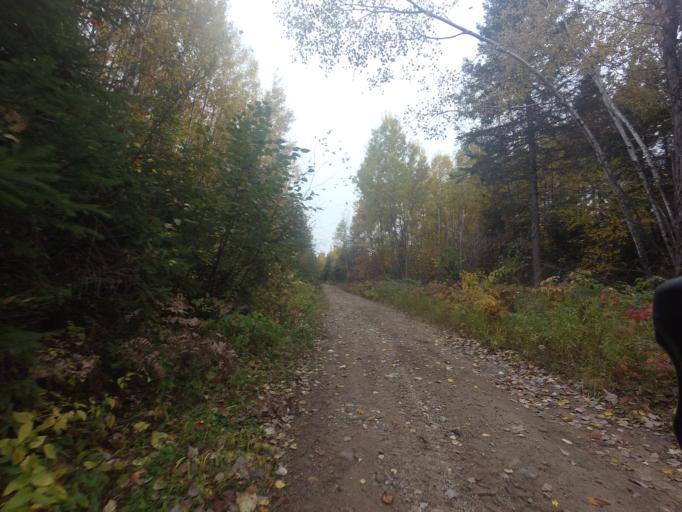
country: CA
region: Ontario
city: Petawawa
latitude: 45.7653
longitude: -77.3692
